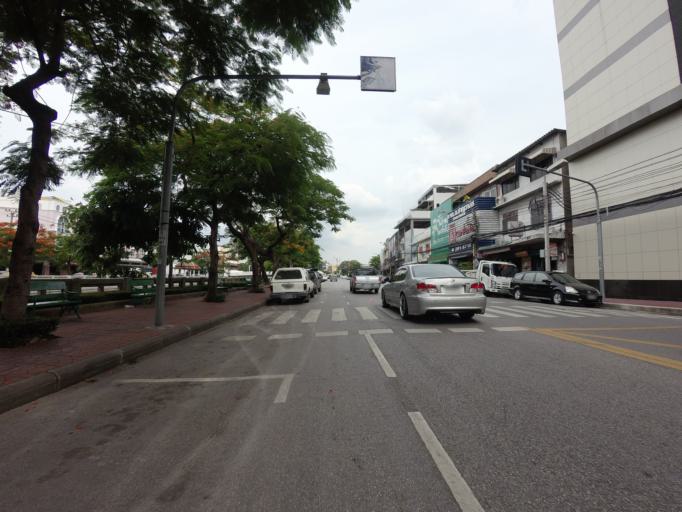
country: TH
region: Bangkok
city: Pom Prap Sattru Phai
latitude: 13.7577
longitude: 100.5152
